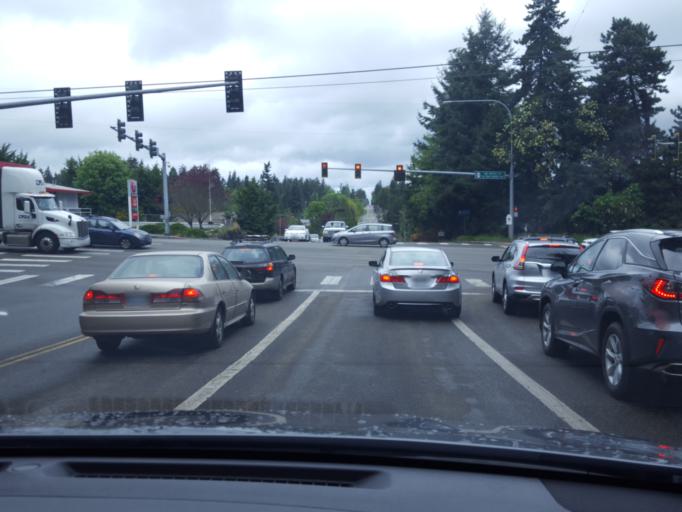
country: US
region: Washington
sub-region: King County
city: Shoreline
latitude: 47.7774
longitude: -122.3353
